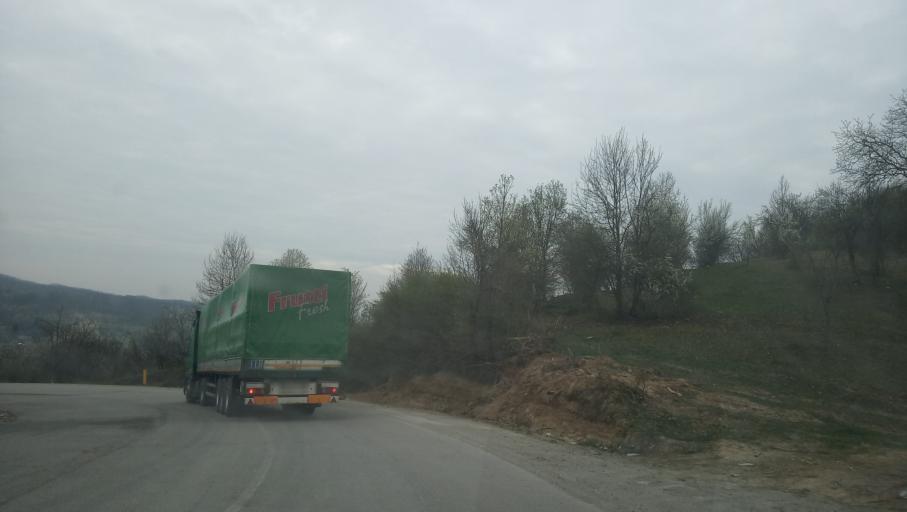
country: RO
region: Arad
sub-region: Comuna Varfurile
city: Varfurile
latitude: 46.3440
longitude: 22.5507
